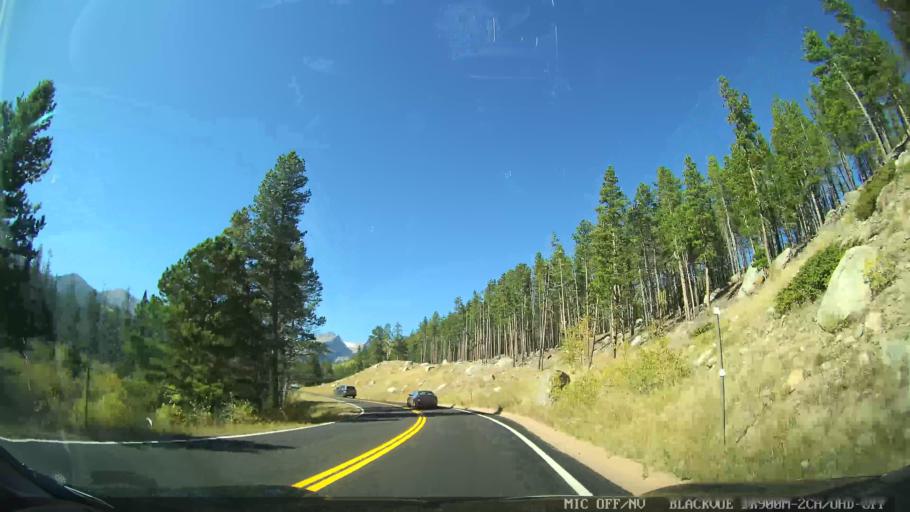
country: US
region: Colorado
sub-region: Larimer County
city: Estes Park
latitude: 40.3257
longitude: -105.6029
